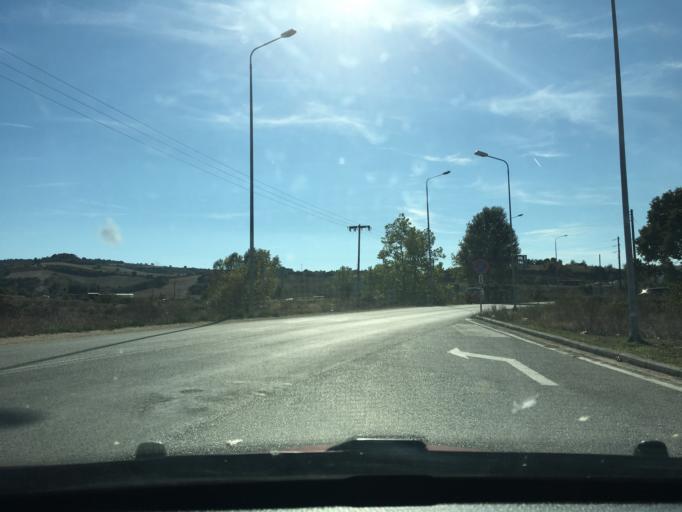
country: GR
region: Central Macedonia
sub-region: Nomos Chalkidikis
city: Ierissos
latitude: 40.3938
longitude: 23.8720
